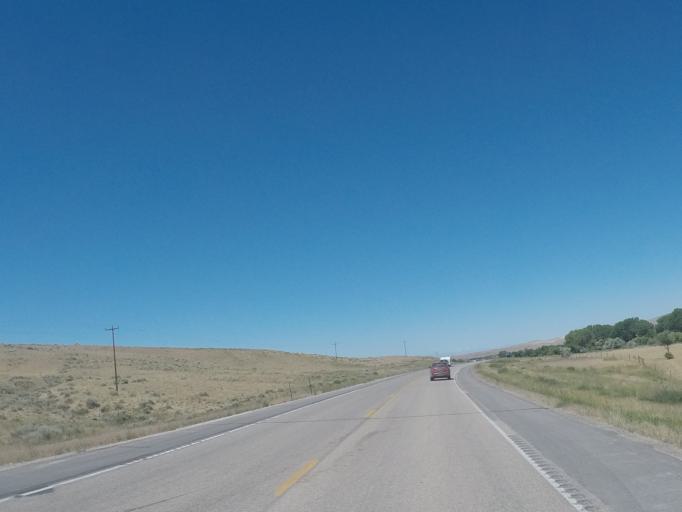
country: US
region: Wyoming
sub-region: Big Horn County
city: Greybull
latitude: 44.5190
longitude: -107.9087
